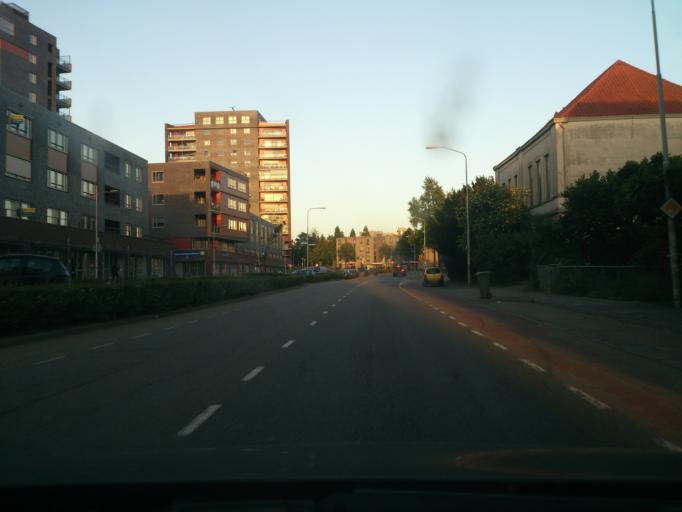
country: NL
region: Gelderland
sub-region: Gemeente Nijmegen
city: Nijmegen
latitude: 51.8495
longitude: 5.8499
